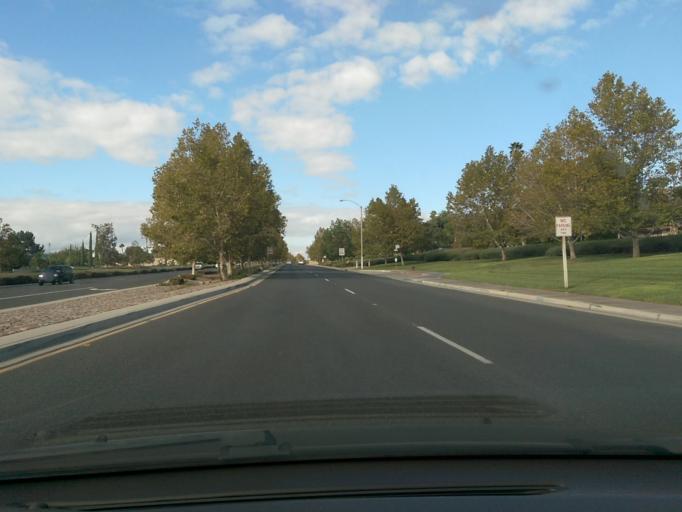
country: US
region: California
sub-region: Riverside County
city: Sunnyslope
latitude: 33.9815
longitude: -117.4401
